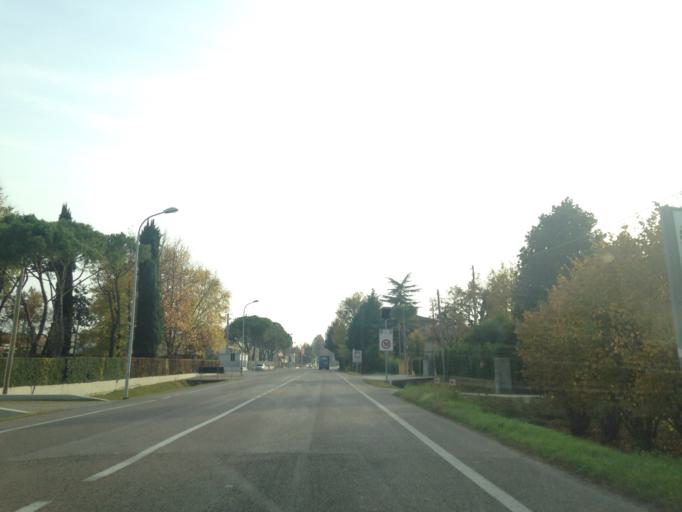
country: IT
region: Veneto
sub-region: Provincia di Treviso
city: Mansue
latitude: 45.8280
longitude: 12.5375
